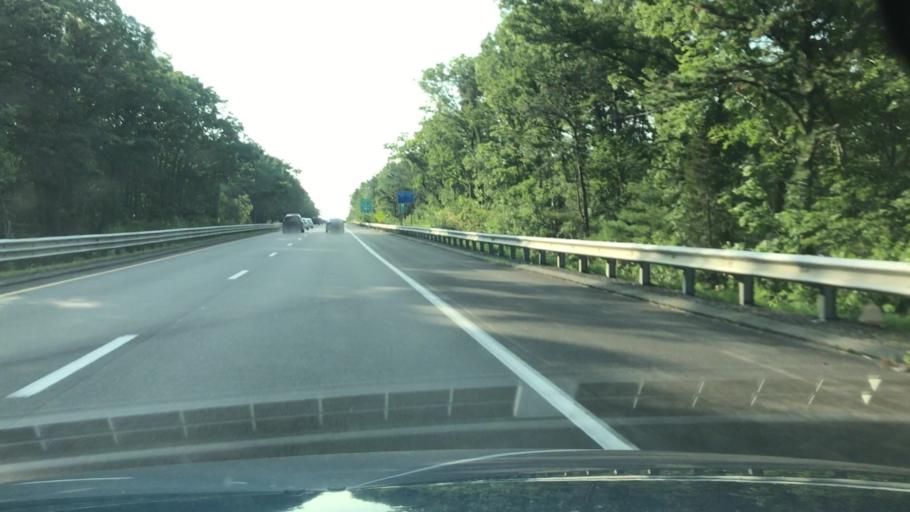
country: US
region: Massachusetts
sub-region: Plymouth County
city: Plymouth
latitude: 41.9309
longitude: -70.6427
